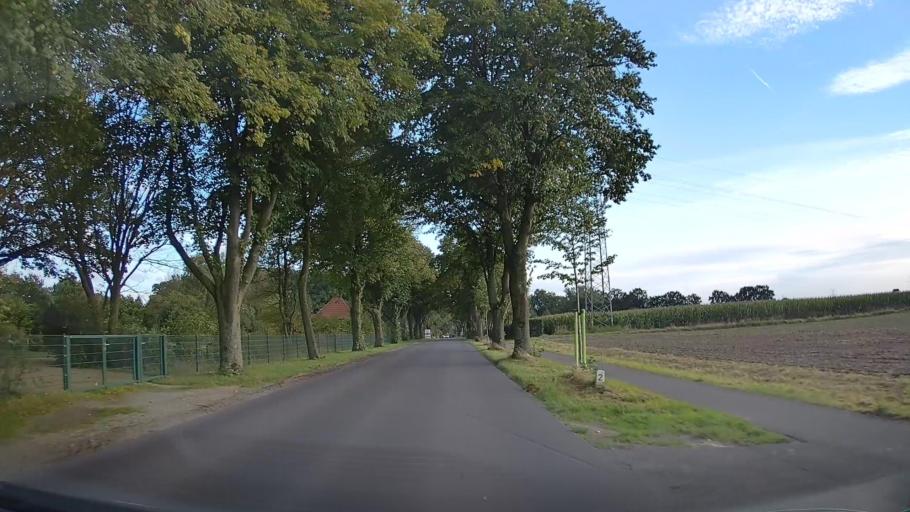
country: DE
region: Lower Saxony
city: Hassendorf
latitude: 53.1166
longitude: 9.2673
